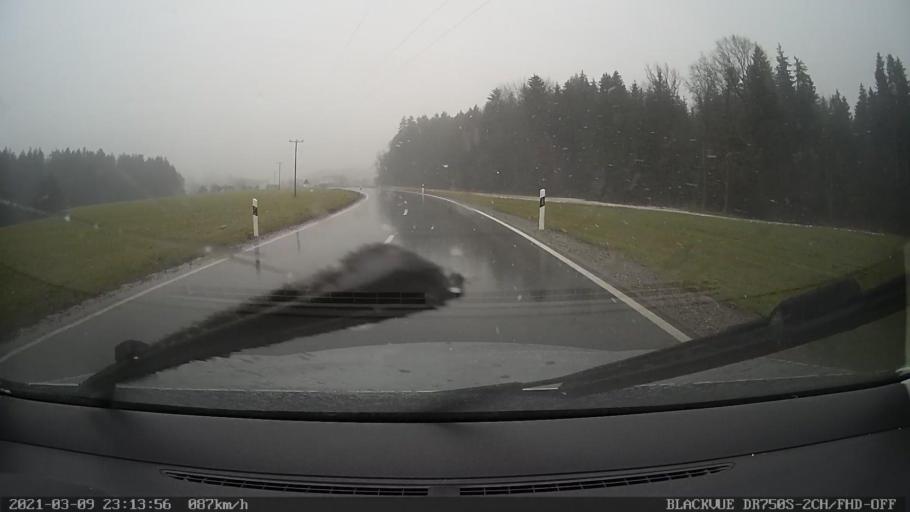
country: DE
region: Bavaria
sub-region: Upper Bavaria
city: Griesstatt
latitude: 47.9829
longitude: 12.2067
